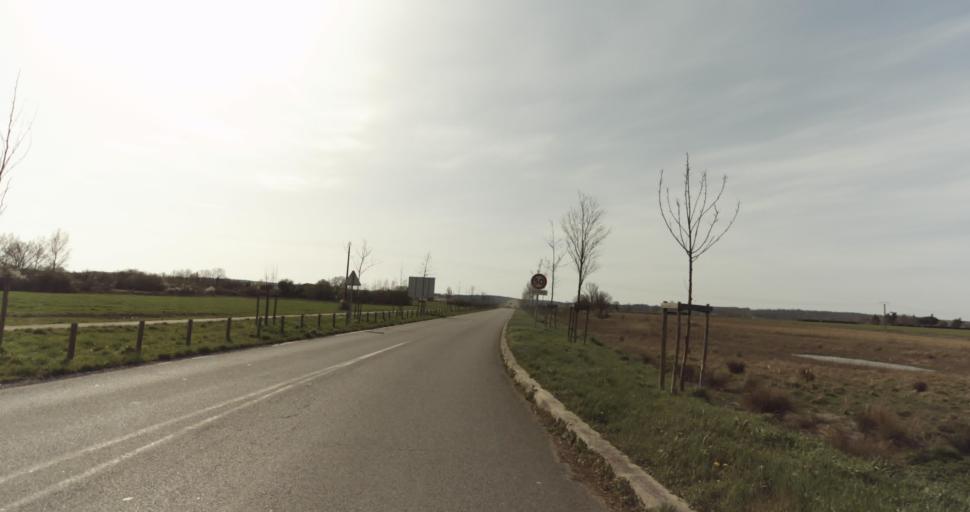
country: FR
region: Midi-Pyrenees
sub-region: Departement de la Haute-Garonne
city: Buzet-sur-Tarn
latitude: 43.7706
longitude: 1.6557
